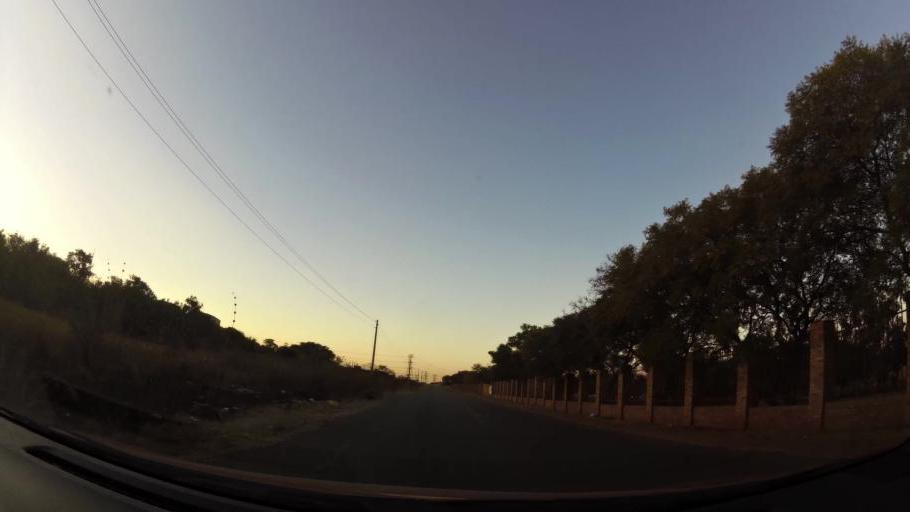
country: ZA
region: North-West
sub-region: Bojanala Platinum District Municipality
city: Rustenburg
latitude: -25.6357
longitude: 27.2014
